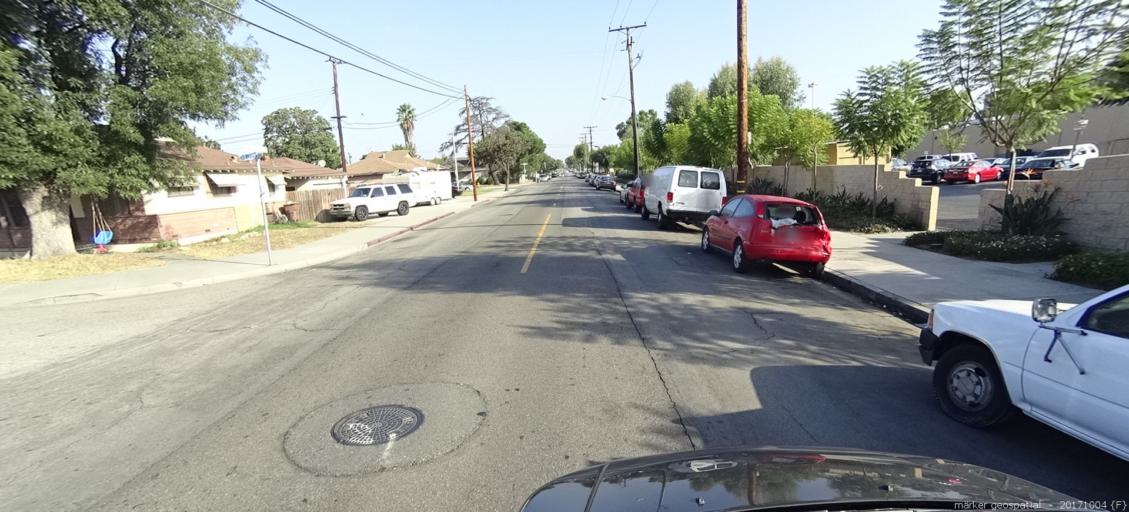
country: US
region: California
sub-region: Orange County
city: Garden Grove
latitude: 33.7768
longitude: -117.9192
